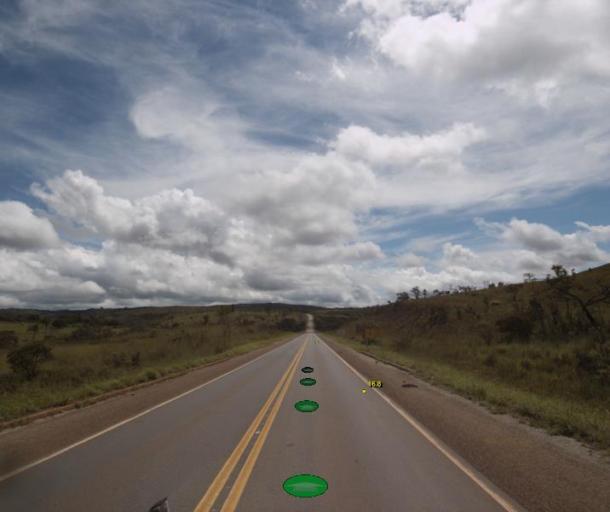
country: BR
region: Federal District
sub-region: Brasilia
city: Brasilia
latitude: -15.7520
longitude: -48.3486
